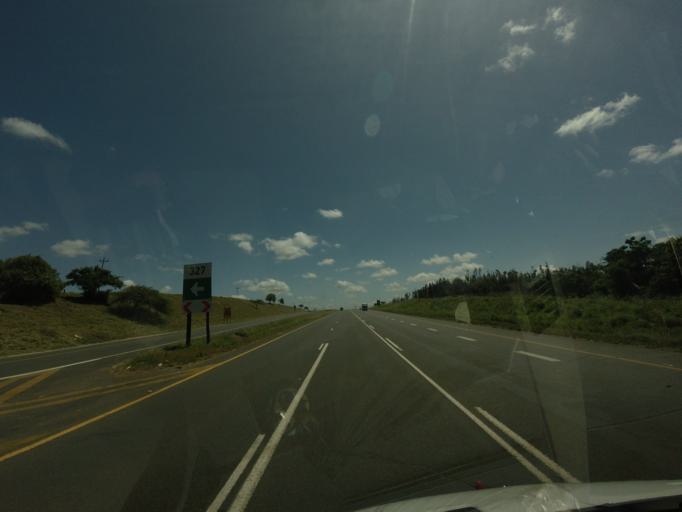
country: ZA
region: KwaZulu-Natal
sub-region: uThungulu District Municipality
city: Empangeni
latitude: -28.7757
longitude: 31.9285
